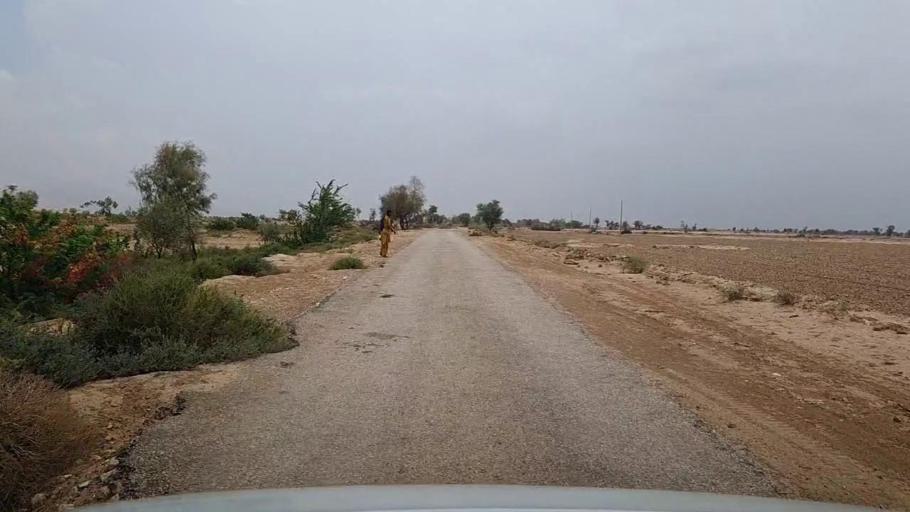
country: PK
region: Sindh
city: Sehwan
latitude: 26.3529
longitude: 67.7955
